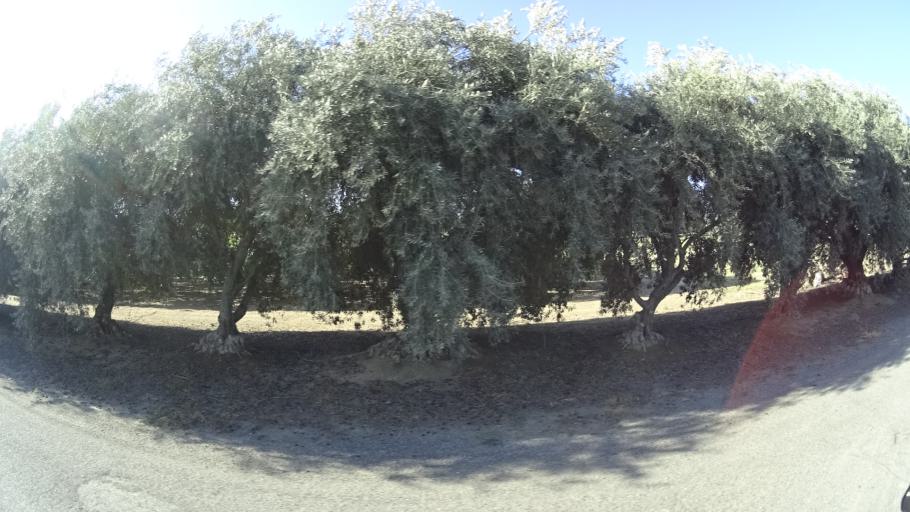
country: US
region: California
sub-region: Glenn County
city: Orland
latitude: 39.7220
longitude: -122.1827
